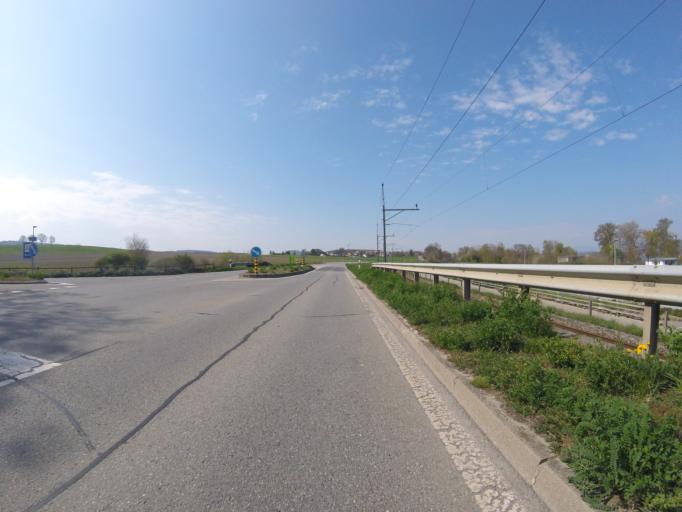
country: CH
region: Fribourg
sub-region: See District
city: Gurwolf
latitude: 46.9138
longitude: 7.0891
